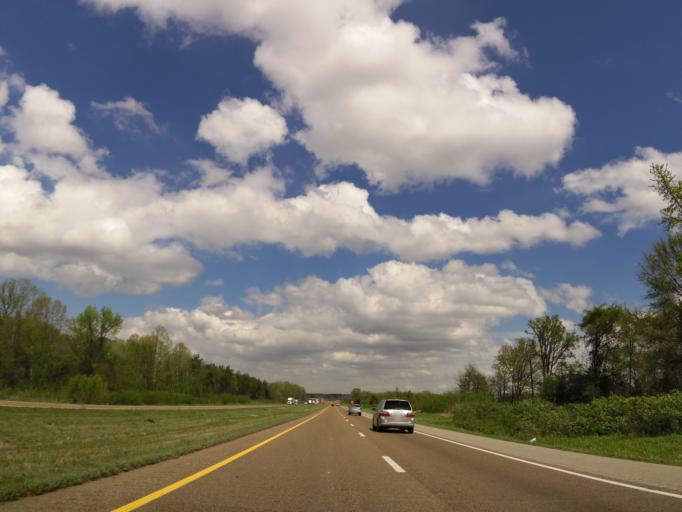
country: US
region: Tennessee
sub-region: Shelby County
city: Arlington
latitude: 35.2815
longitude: -89.6275
